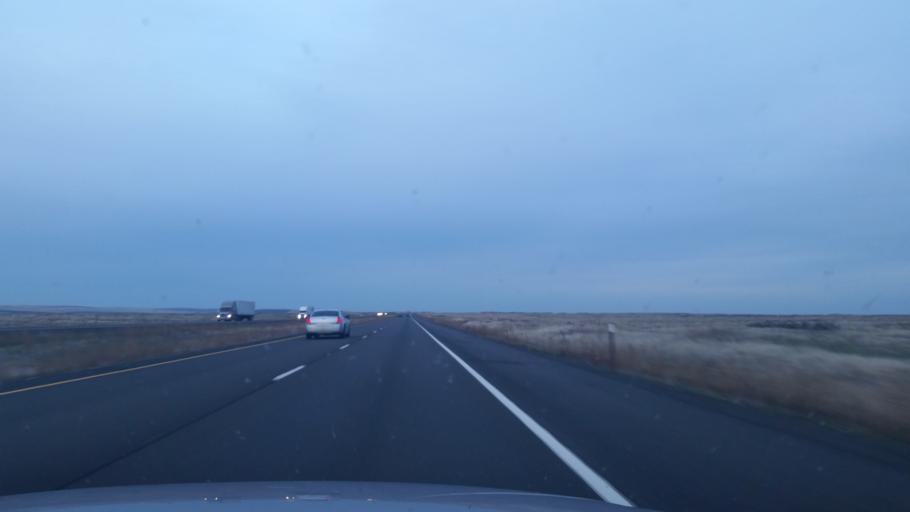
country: US
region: Washington
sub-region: Adams County
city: Ritzville
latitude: 47.2226
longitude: -118.1879
